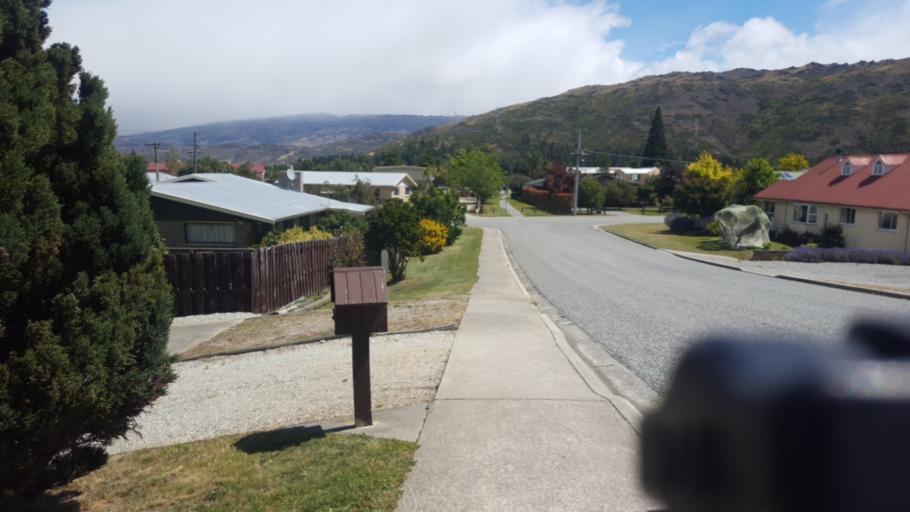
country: NZ
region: Otago
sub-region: Queenstown-Lakes District
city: Wanaka
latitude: -45.1865
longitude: 169.3223
